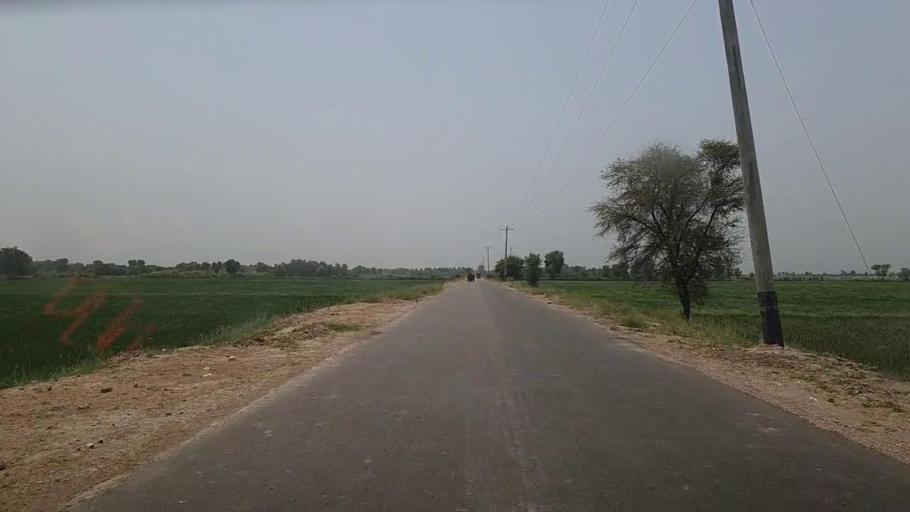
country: PK
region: Sindh
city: Sita Road
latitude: 27.0499
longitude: 67.9017
